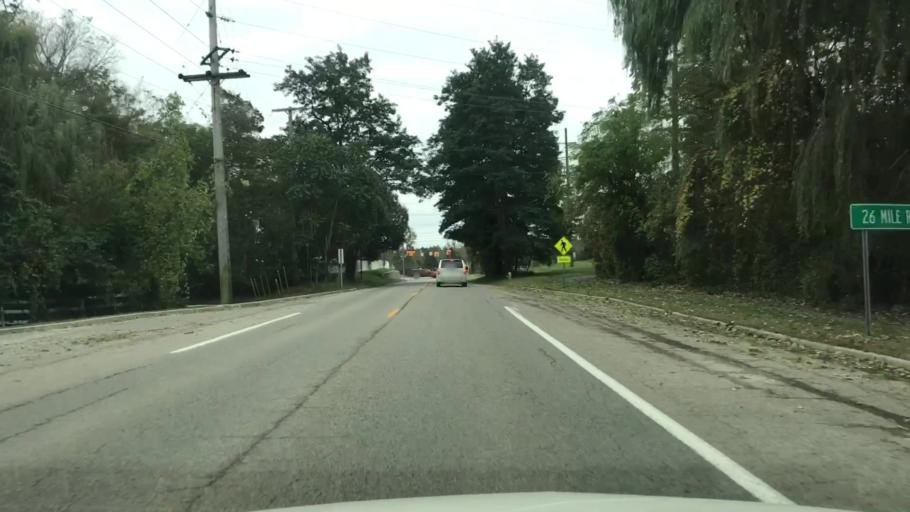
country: US
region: Michigan
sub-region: Macomb County
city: Shelby
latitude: 42.7147
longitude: -83.0560
